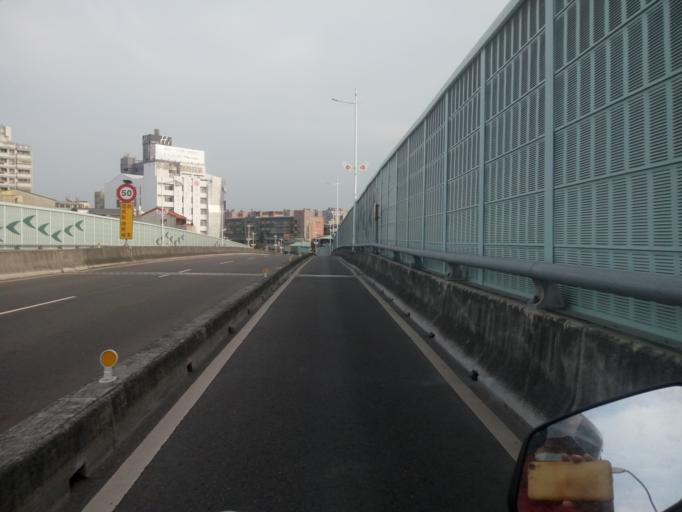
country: TW
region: Taiwan
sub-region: Chiayi
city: Jiayi Shi
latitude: 23.4739
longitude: 120.4359
